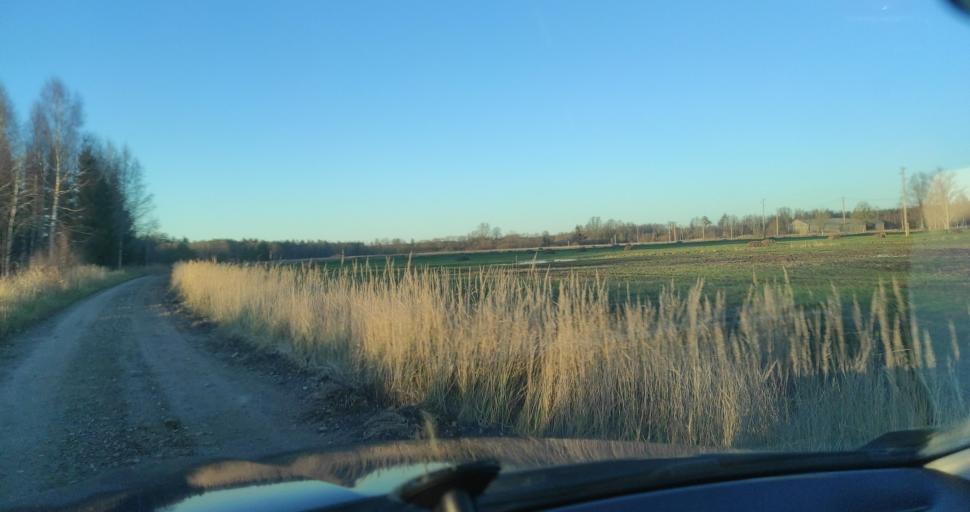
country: LV
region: Dundaga
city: Dundaga
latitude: 57.3875
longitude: 22.0879
